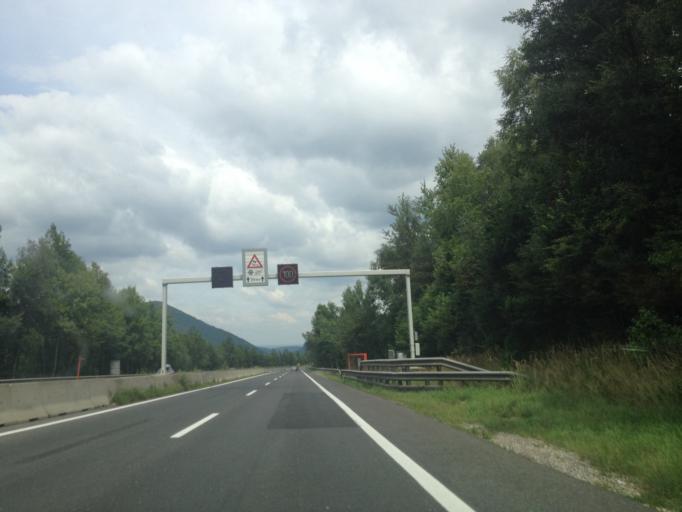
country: AT
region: Lower Austria
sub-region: Politischer Bezirk Neunkirchen
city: Edlitz
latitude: 47.5966
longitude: 16.1242
